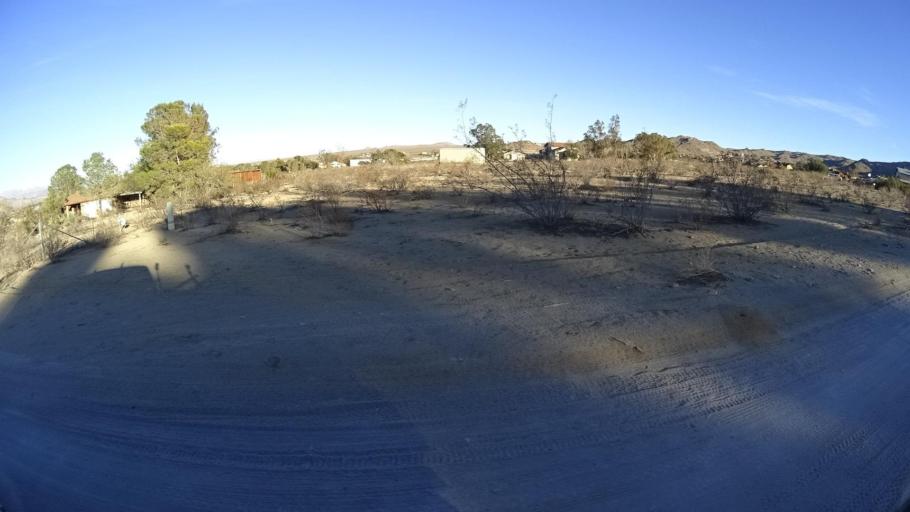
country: US
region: California
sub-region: Kern County
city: Ridgecrest
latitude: 35.5851
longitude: -117.6612
